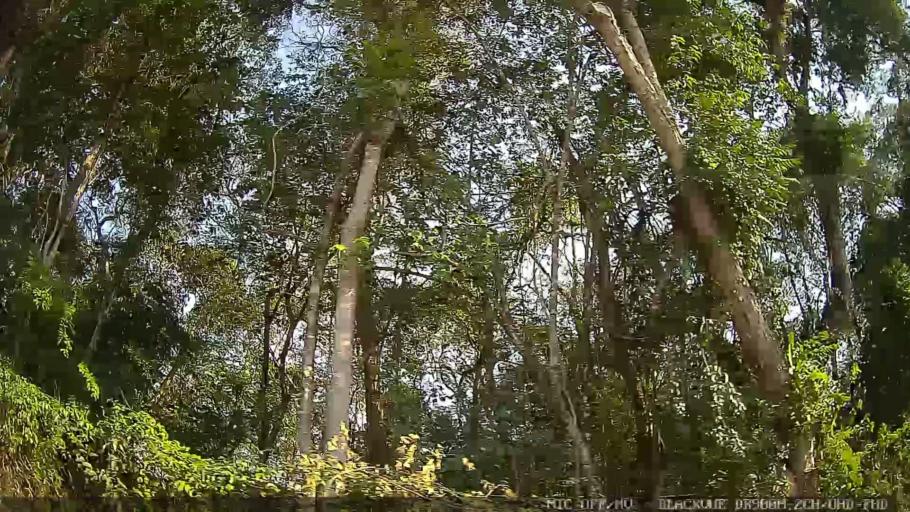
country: BR
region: Sao Paulo
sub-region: Itatiba
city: Itatiba
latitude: -22.9886
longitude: -46.8335
